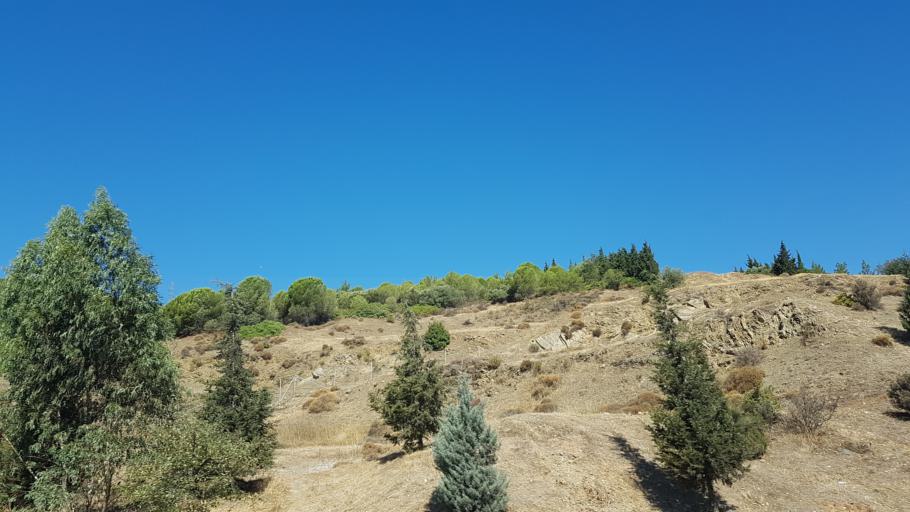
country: TR
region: Izmir
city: Buca
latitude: 38.4056
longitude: 27.2326
